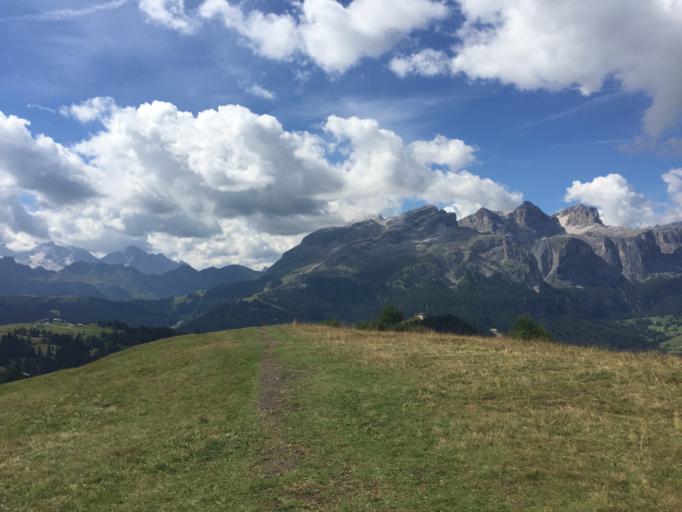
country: IT
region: Trentino-Alto Adige
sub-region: Bolzano
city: Corvara in Badia
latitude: 46.5636
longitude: 11.9046
